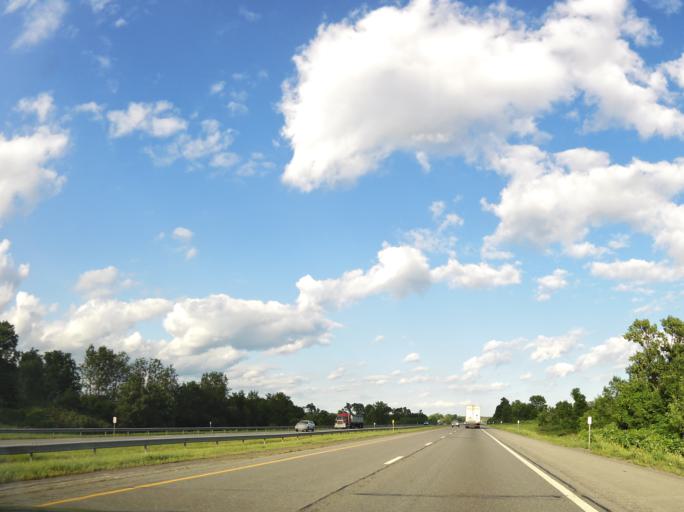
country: US
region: New York
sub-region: Genesee County
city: Oakfield
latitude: 43.0148
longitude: -78.2973
